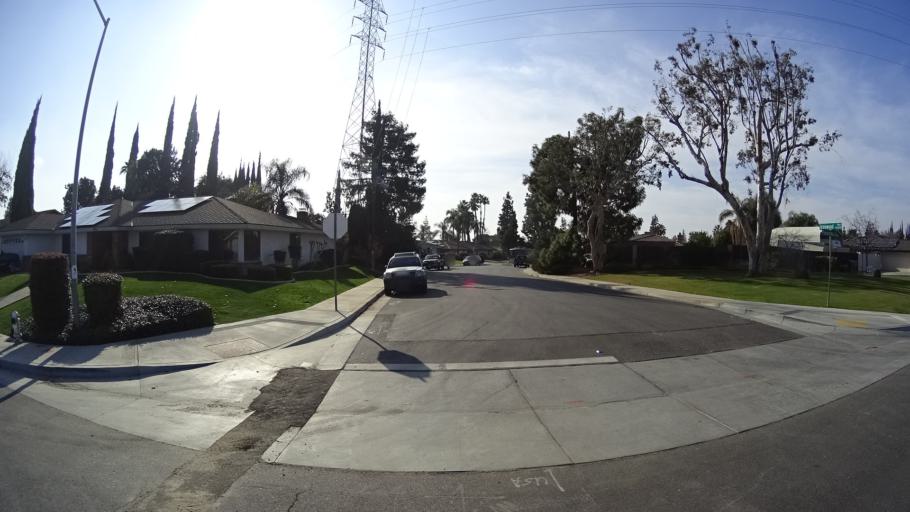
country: US
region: California
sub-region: Kern County
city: Oildale
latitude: 35.4088
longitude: -118.9398
